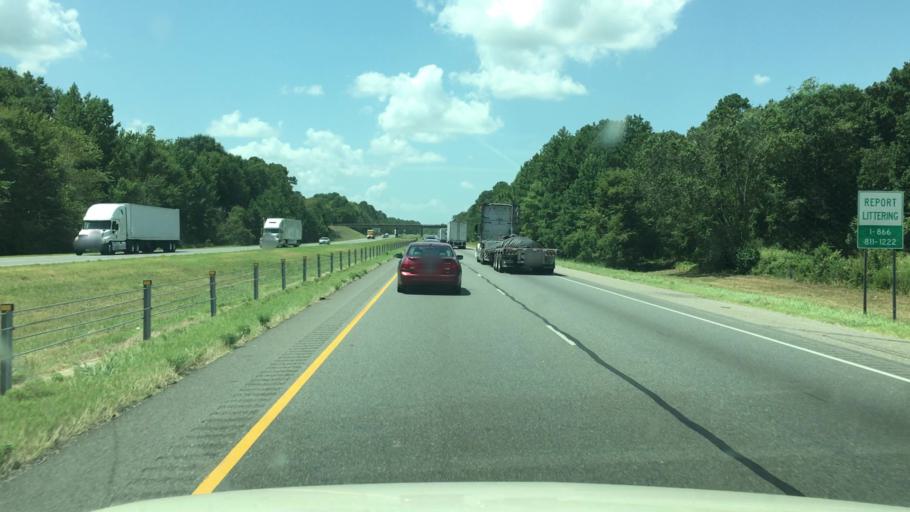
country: US
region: Arkansas
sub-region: Miller County
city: Texarkana
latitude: 33.4914
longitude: -93.9692
